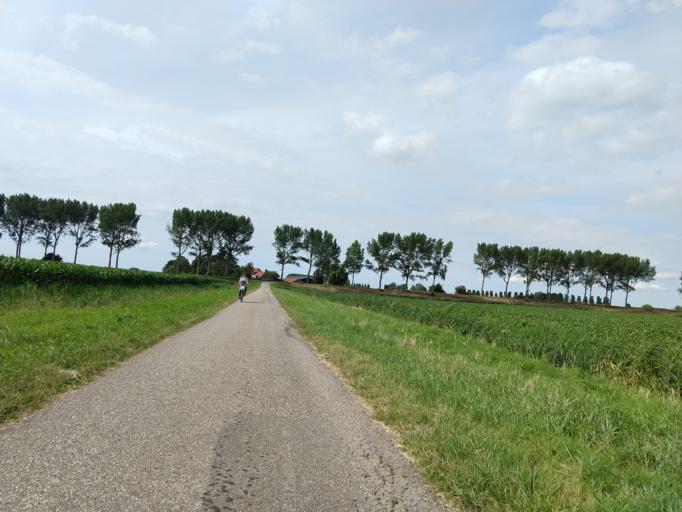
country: NL
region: North Brabant
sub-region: Gemeente Steenbergen
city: Dinteloord
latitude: 51.6725
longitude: 4.3269
